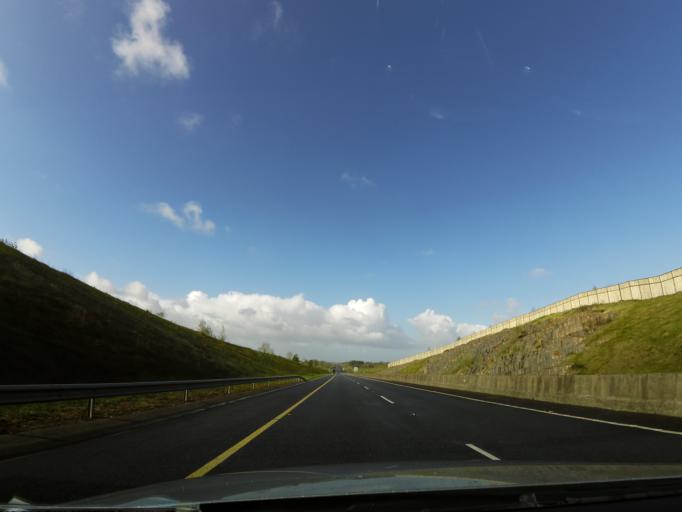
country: IE
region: Munster
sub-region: North Tipperary
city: Newport
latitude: 52.7453
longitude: -8.4346
